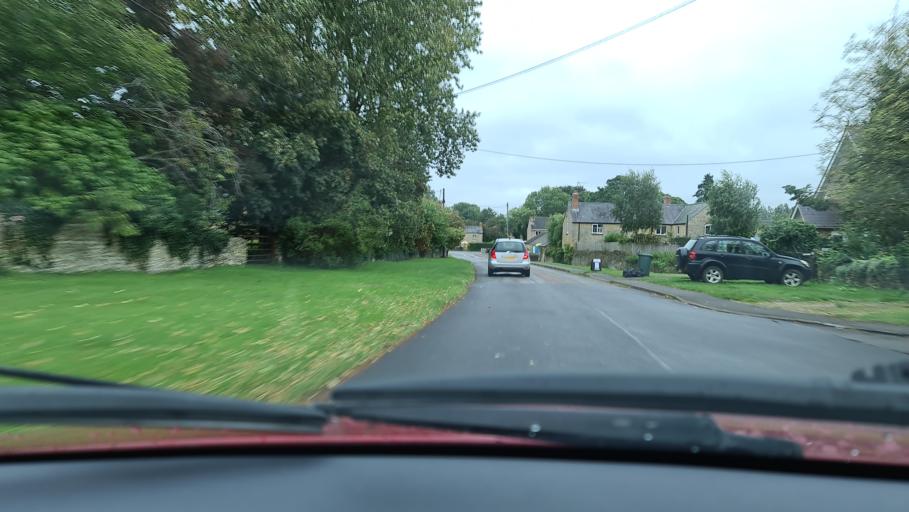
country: GB
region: England
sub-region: Oxfordshire
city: Somerton
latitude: 51.9613
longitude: -1.2356
